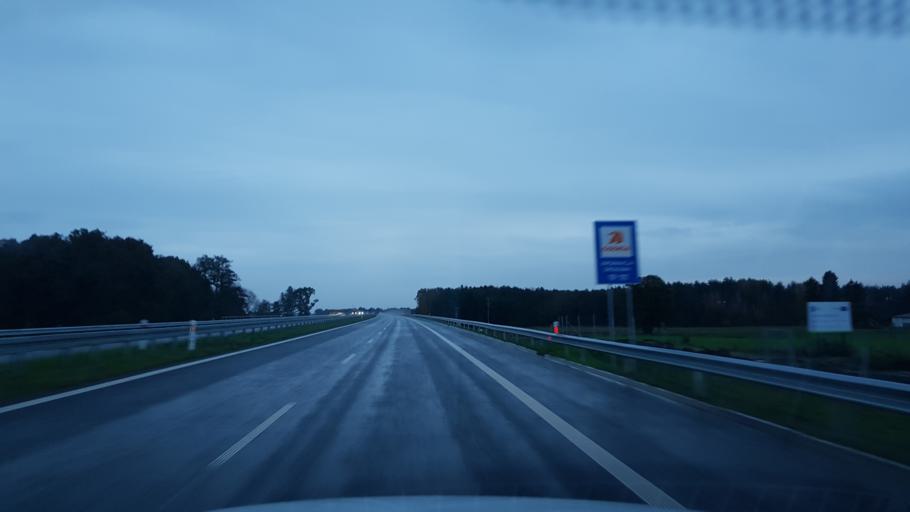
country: PL
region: West Pomeranian Voivodeship
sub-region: Powiat gryficki
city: Brojce
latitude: 53.9552
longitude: 15.4143
